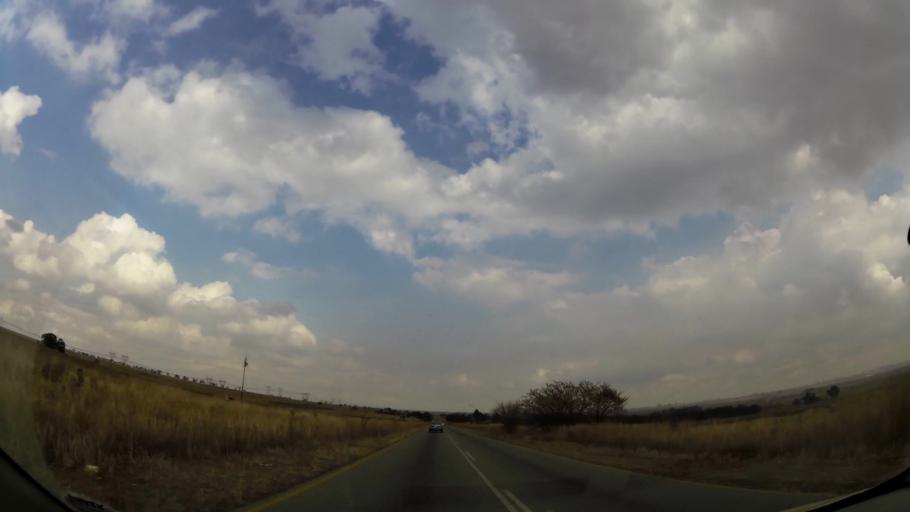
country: ZA
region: Gauteng
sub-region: Sedibeng District Municipality
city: Vanderbijlpark
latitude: -26.7806
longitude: 27.9184
